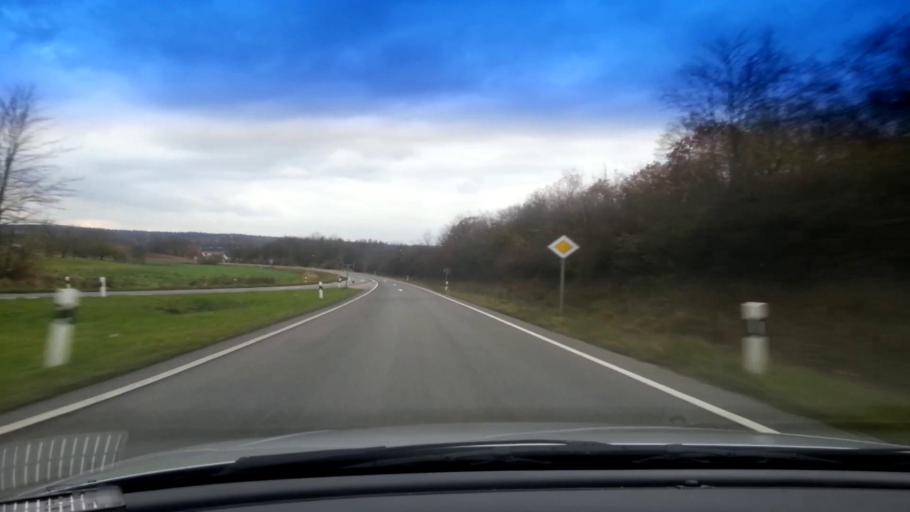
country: DE
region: Bavaria
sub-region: Upper Franconia
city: Stegaurach
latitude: 49.8661
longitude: 10.8599
